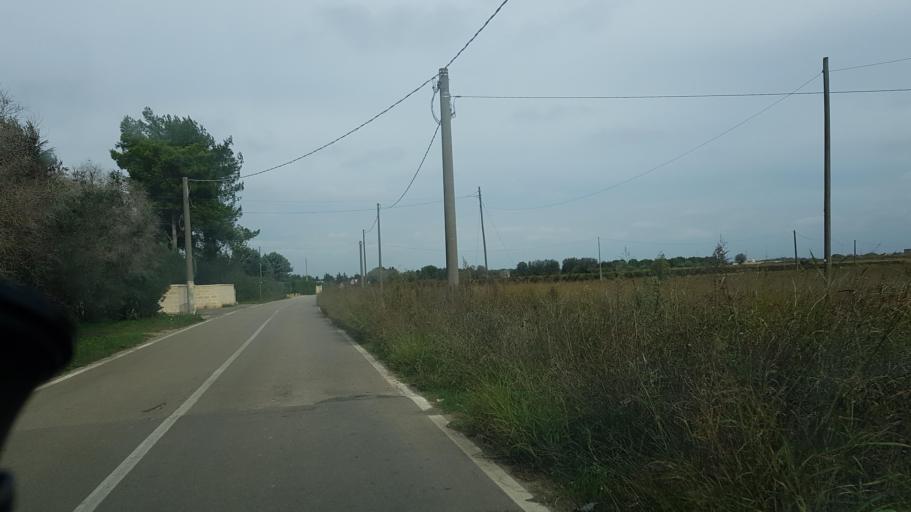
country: IT
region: Apulia
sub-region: Provincia di Lecce
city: Guagnano
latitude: 40.4091
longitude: 17.9496
